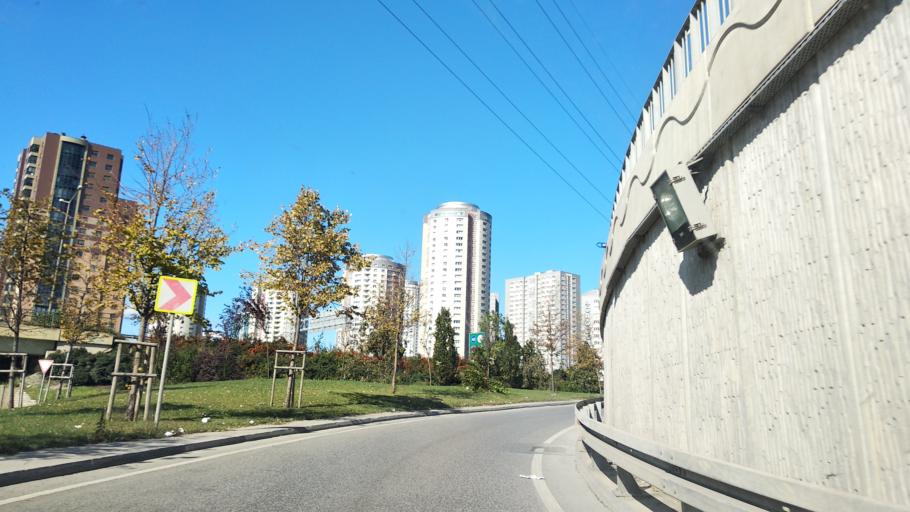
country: TR
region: Istanbul
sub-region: Atasehir
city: Atasehir
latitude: 40.9854
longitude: 29.1065
